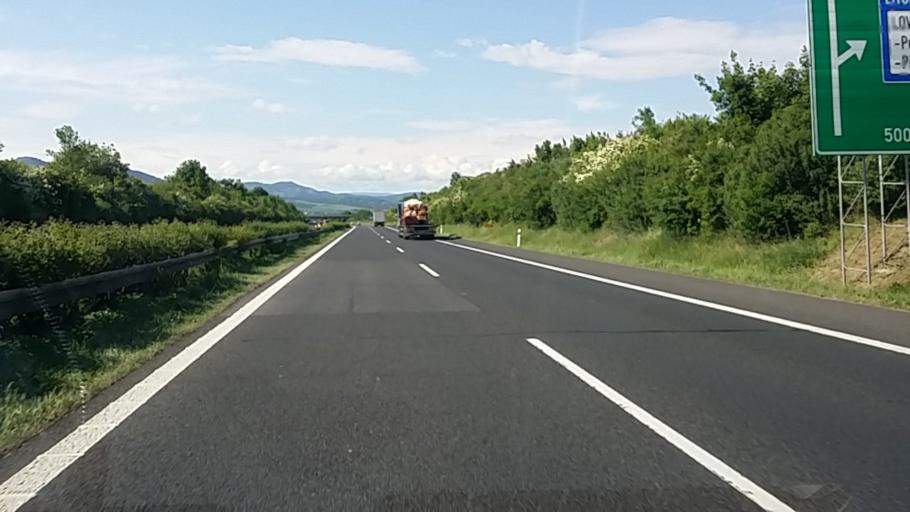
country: CZ
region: Ustecky
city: Lovosice
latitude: 50.4882
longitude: 14.0764
